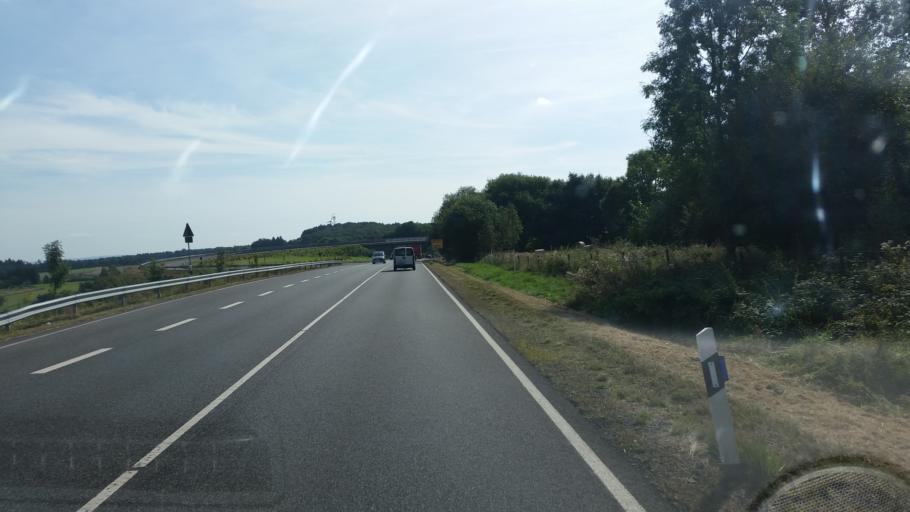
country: DE
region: Rheinland-Pfalz
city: Hartlingen
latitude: 50.5322
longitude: 7.8852
